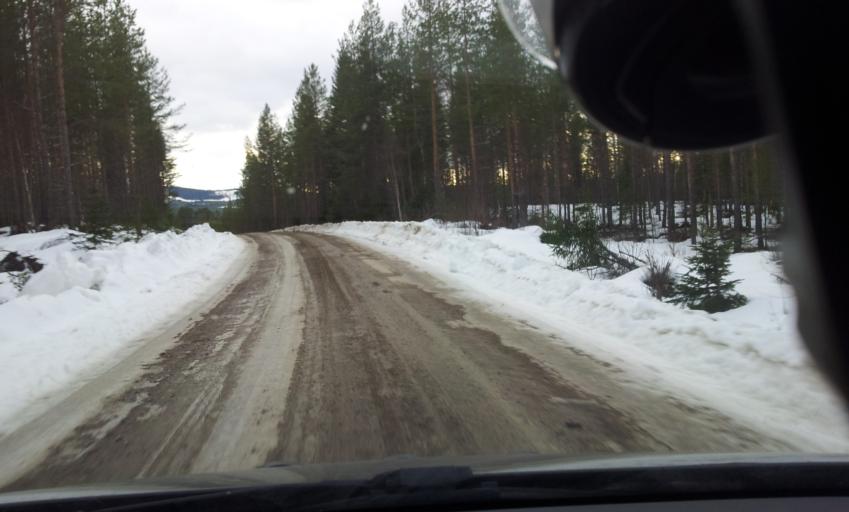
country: SE
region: Vaesternorrland
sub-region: Ange Kommun
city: Ange
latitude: 62.1903
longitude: 15.6786
